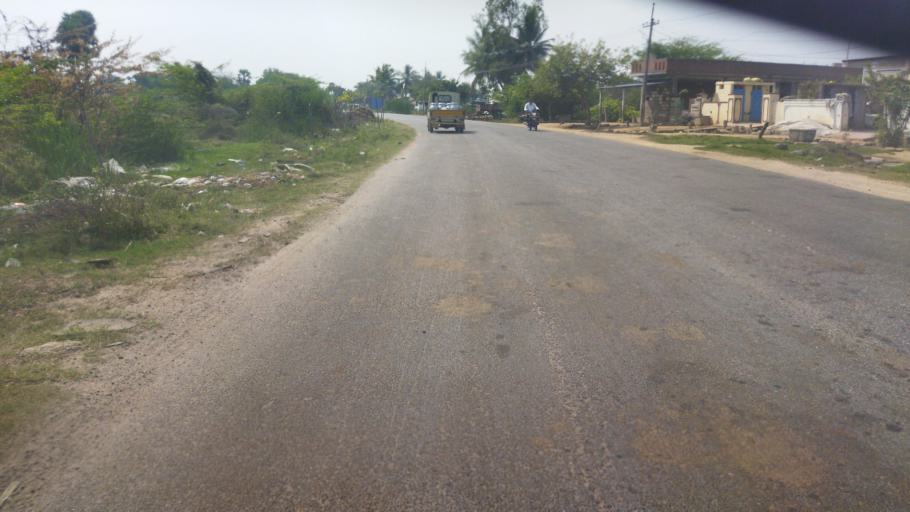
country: IN
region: Telangana
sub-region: Nalgonda
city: Nalgonda
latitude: 17.1520
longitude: 79.3106
